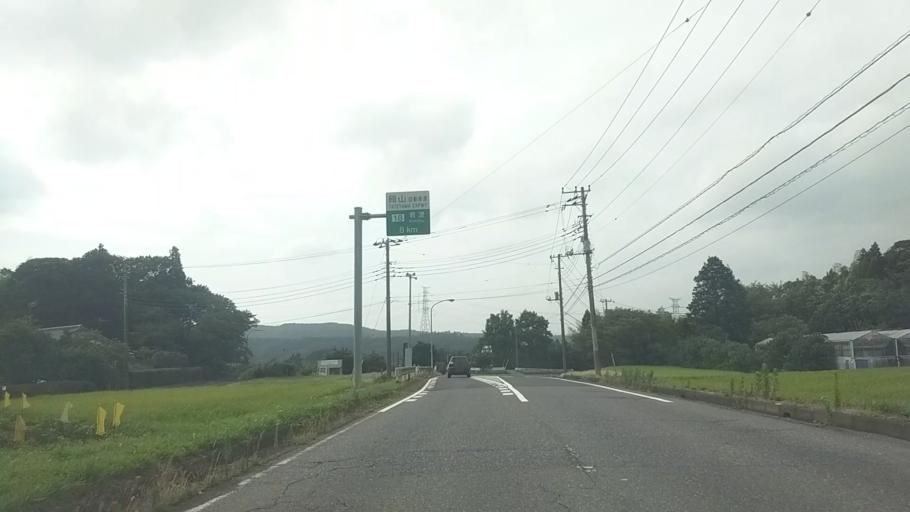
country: JP
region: Chiba
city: Kimitsu
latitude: 35.2785
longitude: 139.9908
